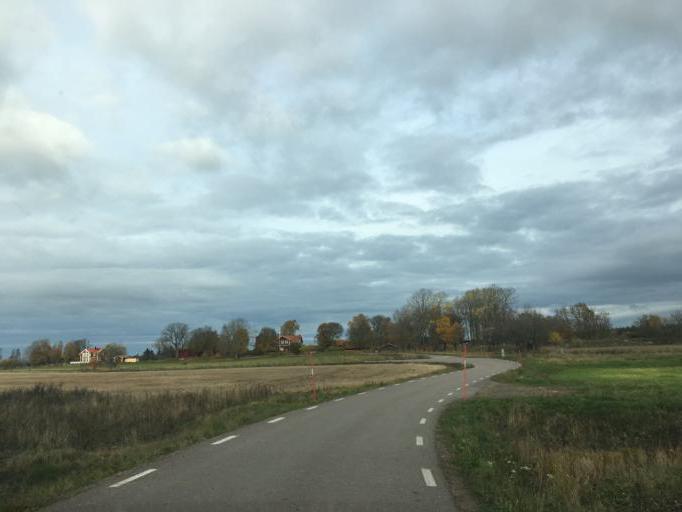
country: SE
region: Soedermanland
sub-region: Eskilstuna Kommun
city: Kvicksund
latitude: 59.5469
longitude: 16.3577
